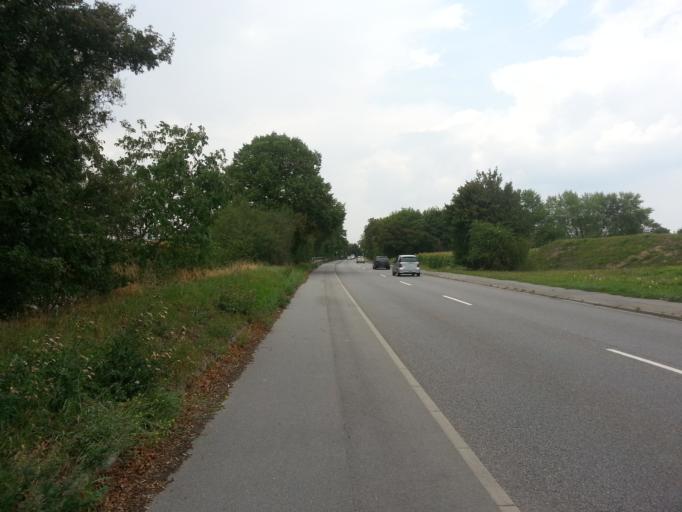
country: DE
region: Baden-Wuerttemberg
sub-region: Karlsruhe Region
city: Ladenburg
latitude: 49.4764
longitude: 8.5898
